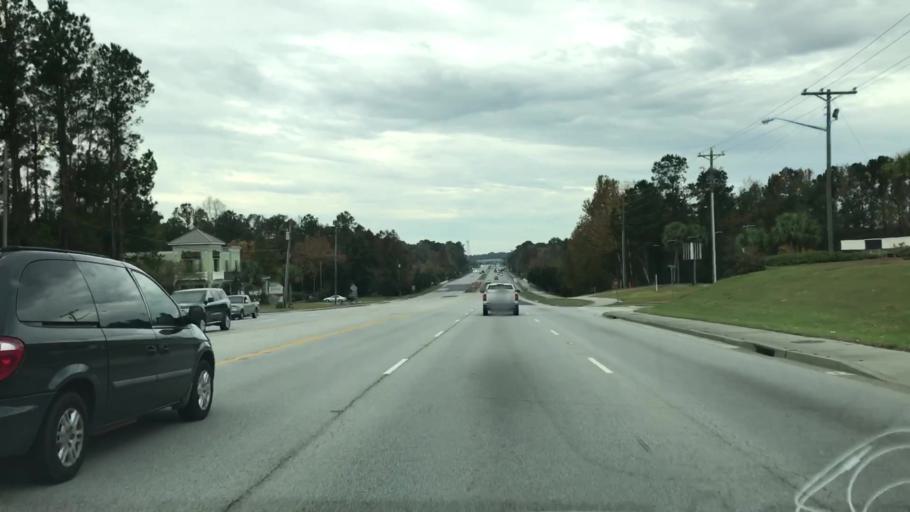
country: US
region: South Carolina
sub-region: Berkeley County
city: Goose Creek
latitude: 32.9880
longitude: -80.0406
